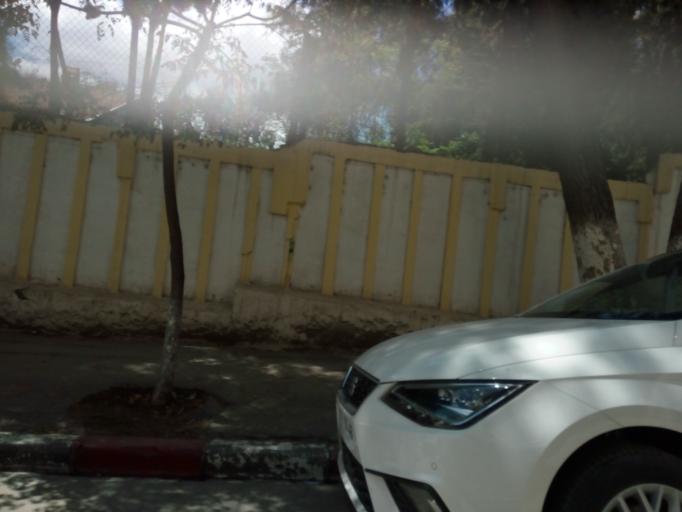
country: DZ
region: Constantine
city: Constantine
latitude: 36.3735
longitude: 6.6198
